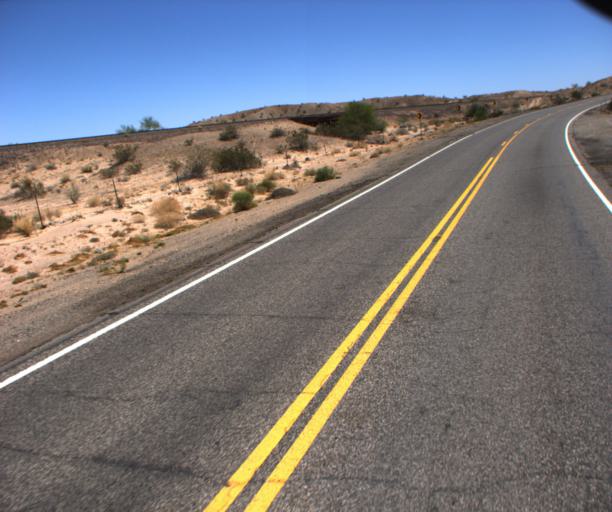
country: US
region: Arizona
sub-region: La Paz County
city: Parker
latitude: 34.0128
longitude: -114.2444
